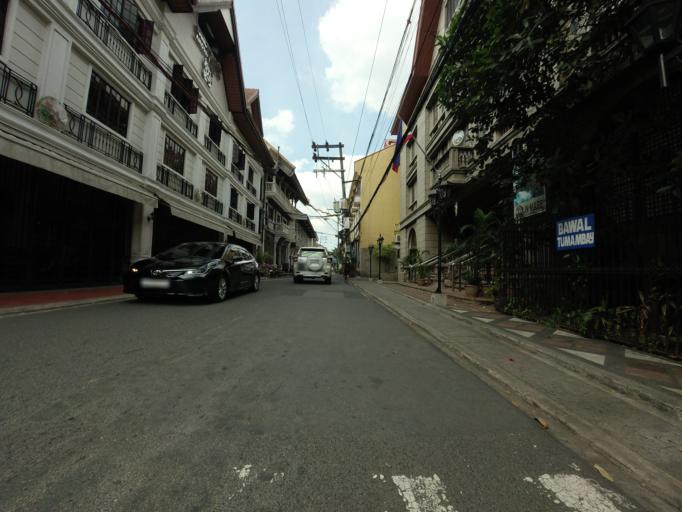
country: PH
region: Metro Manila
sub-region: City of Manila
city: Port Area
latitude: 14.5893
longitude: 120.9763
